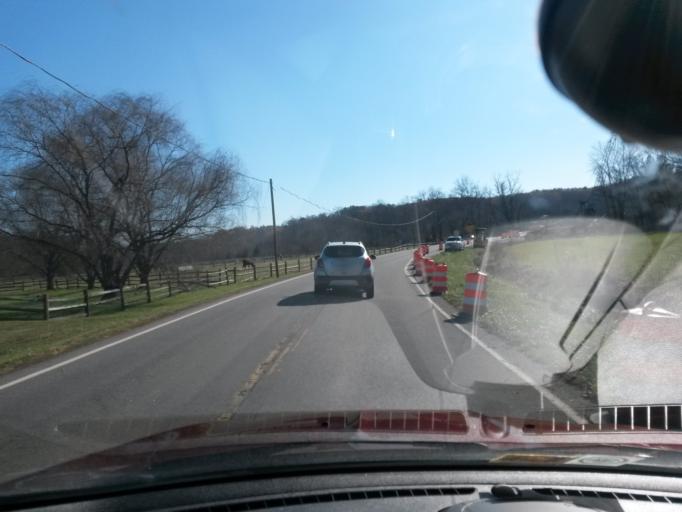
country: US
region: Virginia
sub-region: City of Bedford
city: Bedford
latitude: 37.3912
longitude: -79.5521
